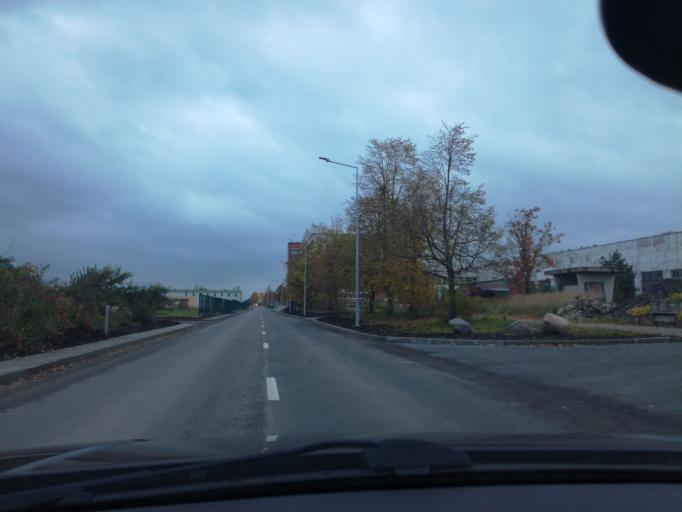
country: LT
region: Alytaus apskritis
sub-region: Alytus
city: Alytus
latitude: 54.4187
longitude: 24.0141
